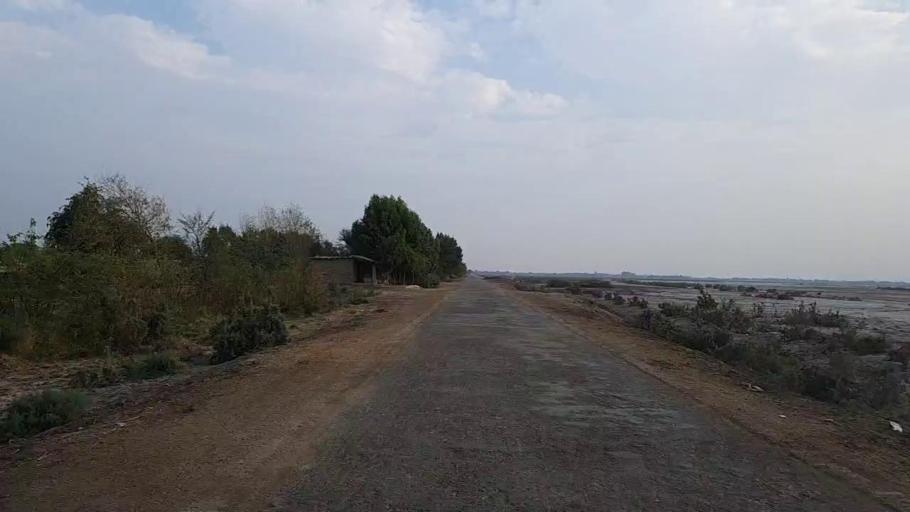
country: PK
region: Sindh
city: Pithoro
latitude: 25.4777
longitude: 69.2669
